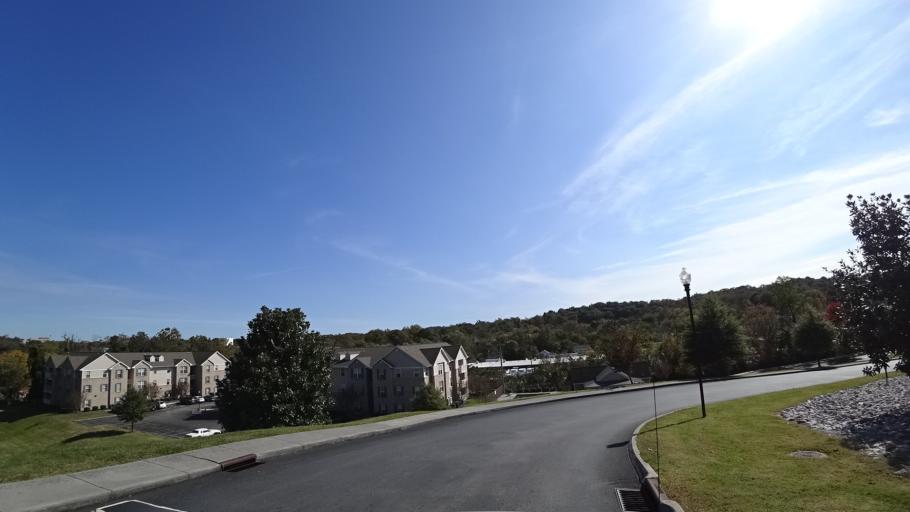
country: US
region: Tennessee
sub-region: Knox County
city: Knoxville
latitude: 35.9524
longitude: -83.9721
